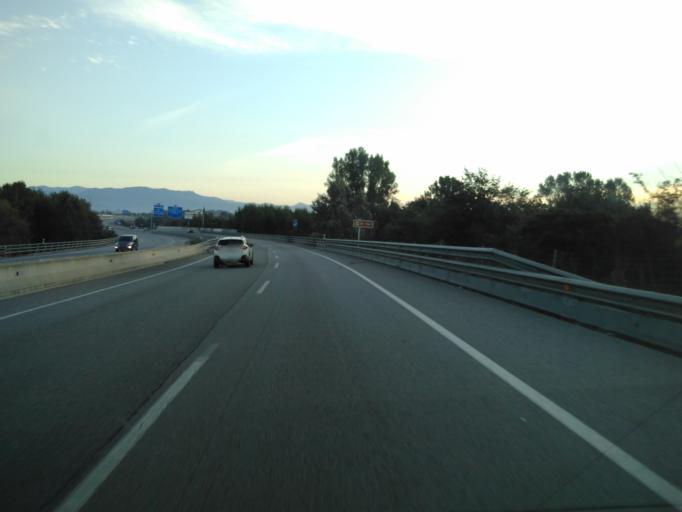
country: ES
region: Catalonia
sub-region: Provincia de Barcelona
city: Santa Cecilia de Voltrega
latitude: 41.9931
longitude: 2.2485
